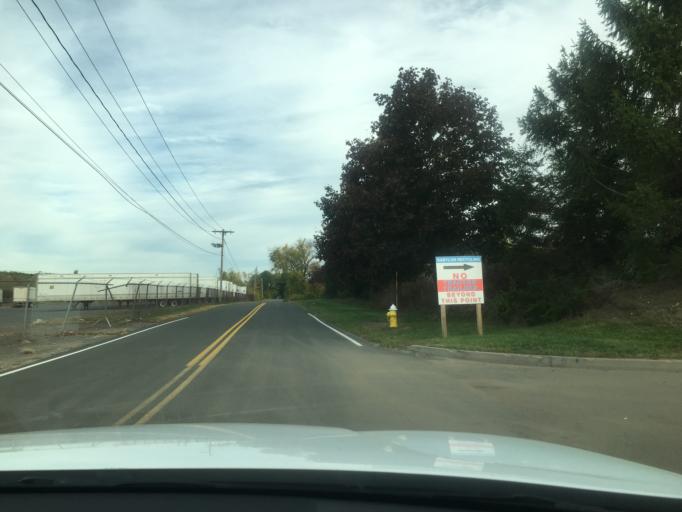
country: US
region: Connecticut
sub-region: Hartford County
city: Windsor Locks
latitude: 41.9453
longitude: -72.6228
